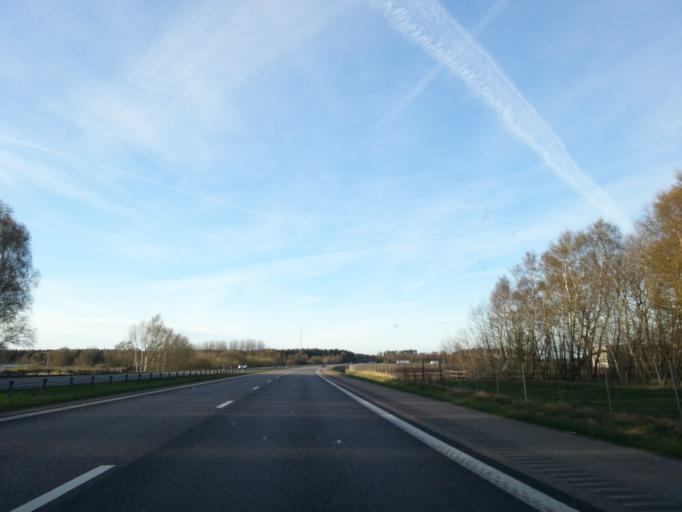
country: SE
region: Halland
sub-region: Laholms Kommun
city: Mellbystrand
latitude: 56.4690
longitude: 12.9417
